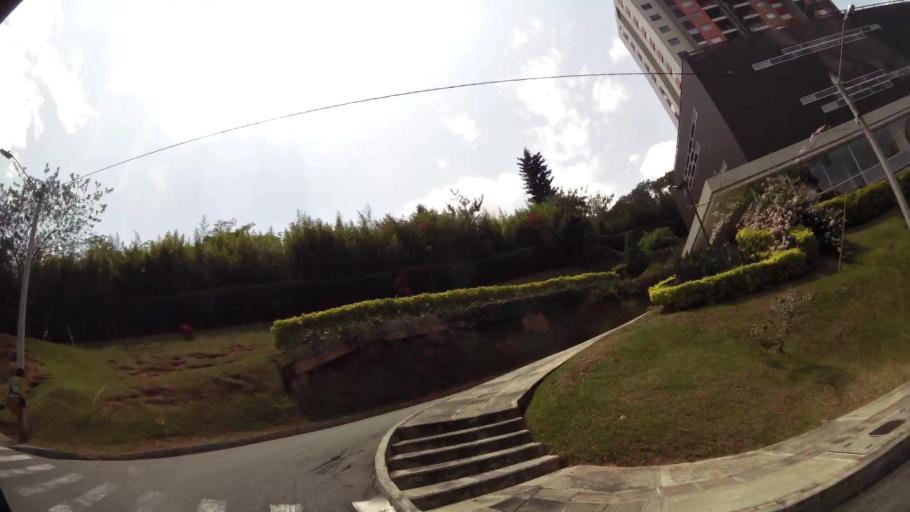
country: CO
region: Antioquia
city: Medellin
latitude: 6.2376
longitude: -75.6098
